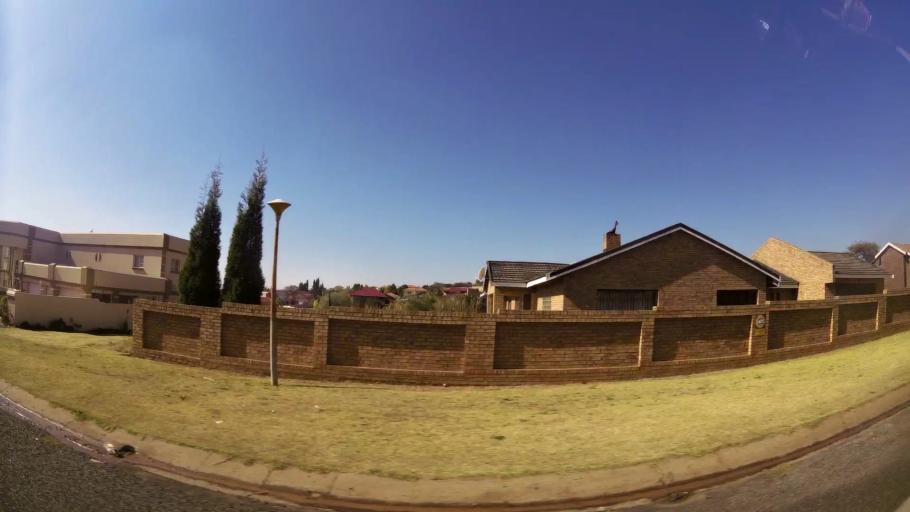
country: ZA
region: Mpumalanga
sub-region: Nkangala District Municipality
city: Witbank
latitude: -25.8620
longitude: 29.2419
